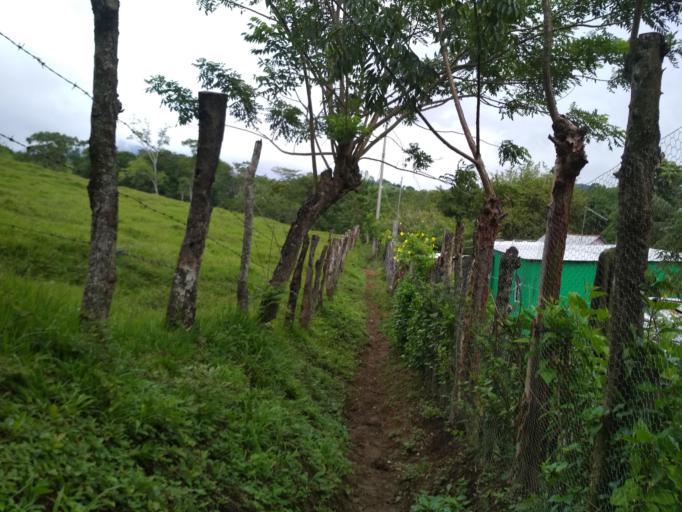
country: MX
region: Veracruz
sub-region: San Andres Tuxtla
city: Soyata
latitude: 18.3958
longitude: -95.3205
